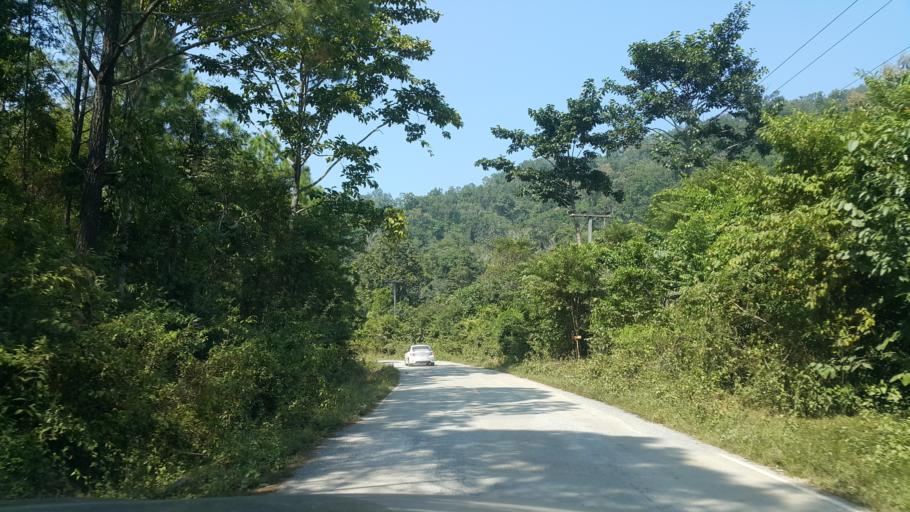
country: TH
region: Chiang Mai
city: Samoeng
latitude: 18.8748
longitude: 98.6236
